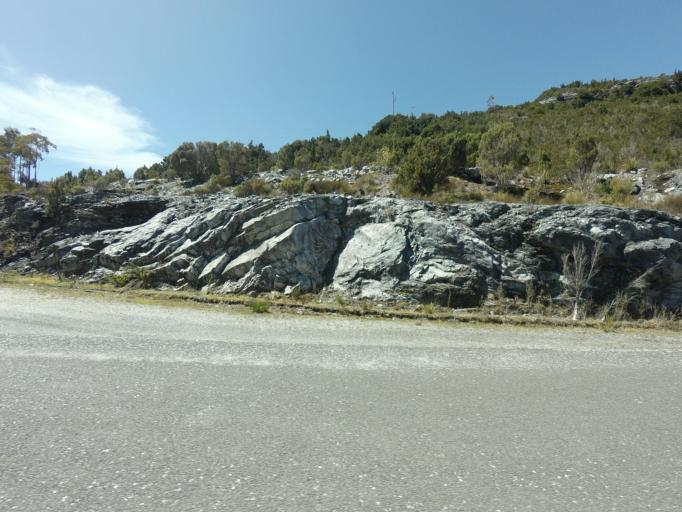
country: AU
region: Tasmania
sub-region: West Coast
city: Queenstown
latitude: -42.7336
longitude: 145.9753
